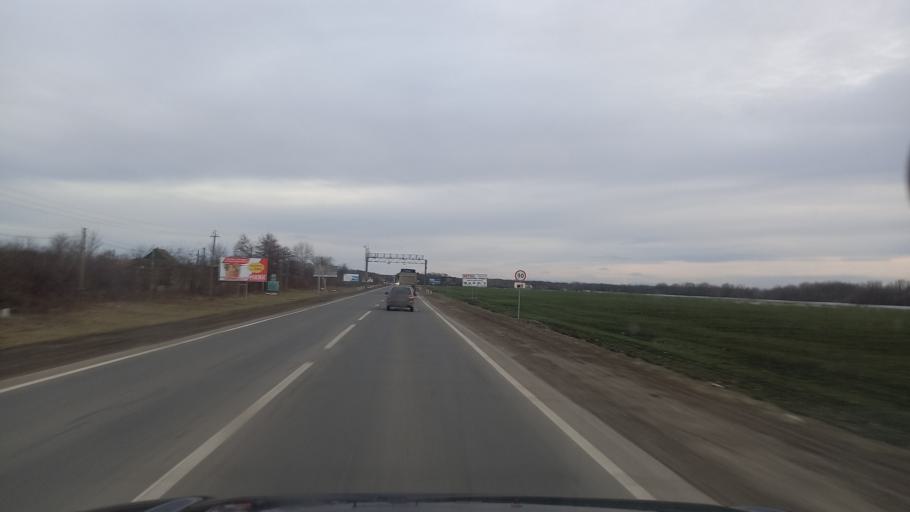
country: RU
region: Krasnodarskiy
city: Belorechensk
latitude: 44.7466
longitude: 39.9275
